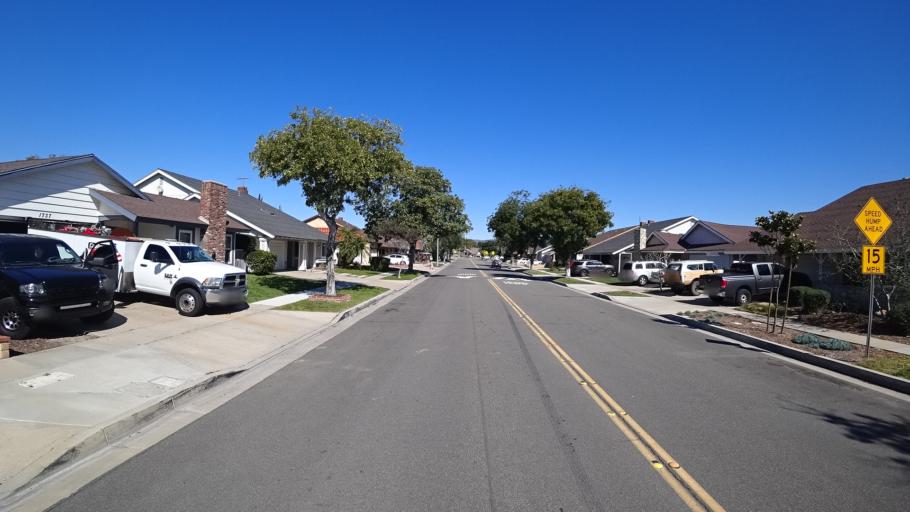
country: US
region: California
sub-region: Orange County
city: Yorba Linda
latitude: 33.8670
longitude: -117.8129
